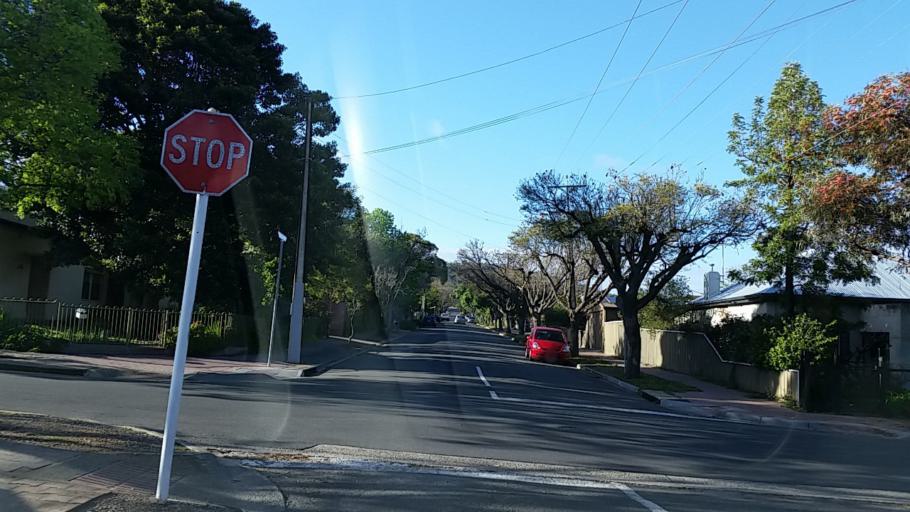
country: AU
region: South Australia
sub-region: Mitcham
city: Clapham
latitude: -34.9851
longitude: 138.6066
